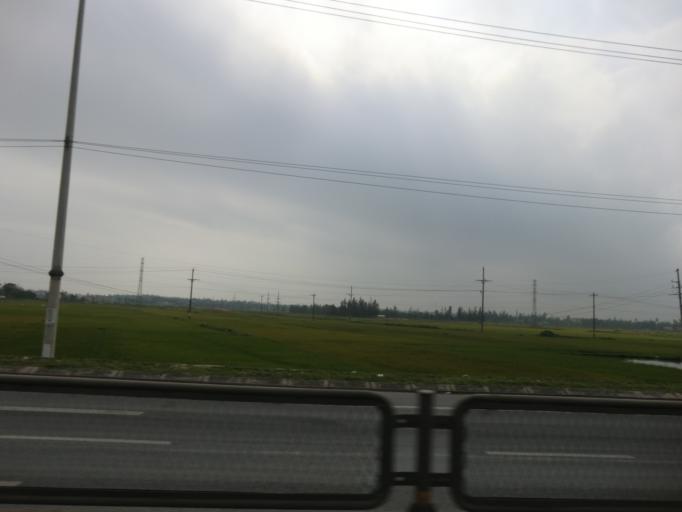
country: VN
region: Quang Binh
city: Ba Don
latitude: 17.7593
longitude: 106.4436
